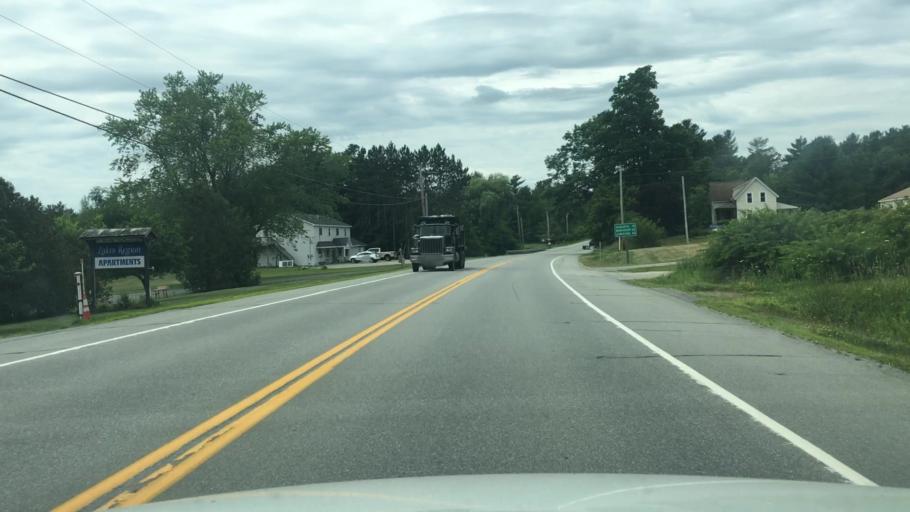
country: US
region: Maine
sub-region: Kennebec County
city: Windsor
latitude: 44.3866
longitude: -69.5966
